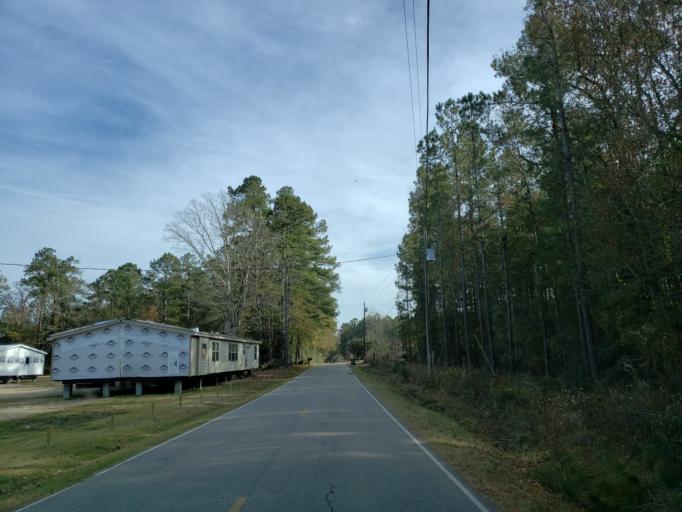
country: US
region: Mississippi
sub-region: Forrest County
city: Rawls Springs
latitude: 31.3947
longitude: -89.3862
